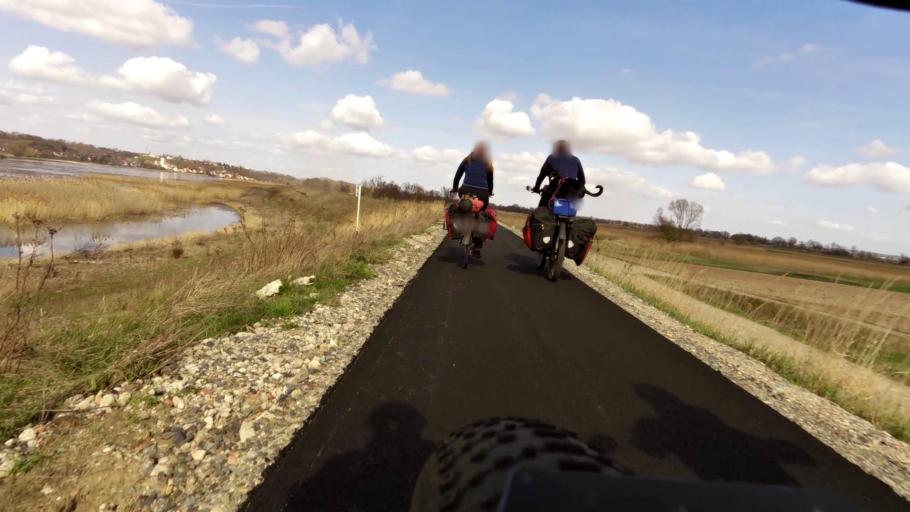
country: DE
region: Brandenburg
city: Lebus
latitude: 52.4138
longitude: 14.5493
